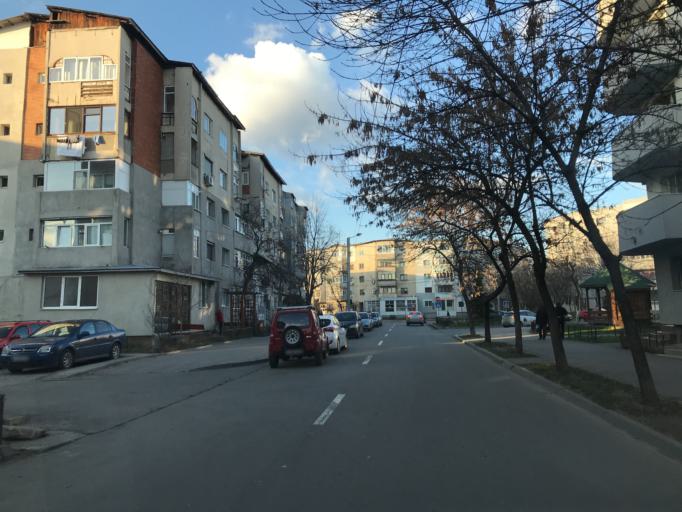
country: RO
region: Olt
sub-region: Municipiul Slatina
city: Slatina
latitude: 44.4225
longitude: 24.3816
